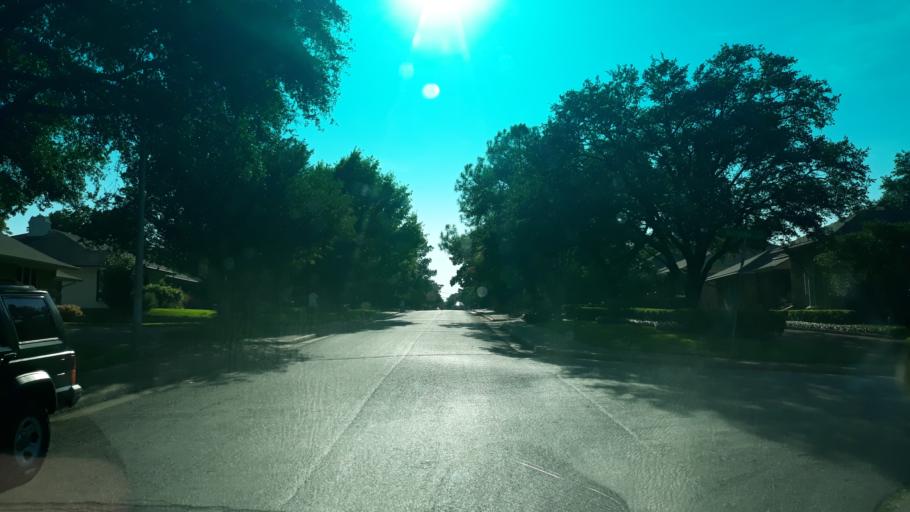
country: US
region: Texas
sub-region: Dallas County
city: Highland Park
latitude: 32.8302
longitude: -96.7500
